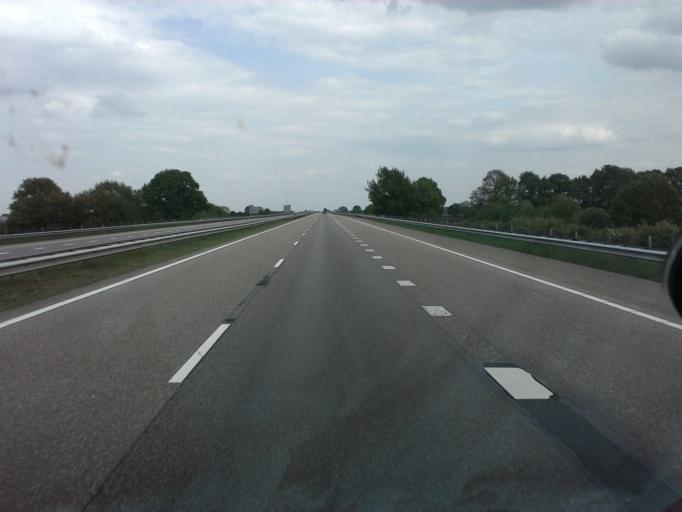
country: NL
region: North Brabant
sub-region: Gemeente Boxmeer
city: Boxmeer
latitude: 51.6624
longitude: 5.9499
